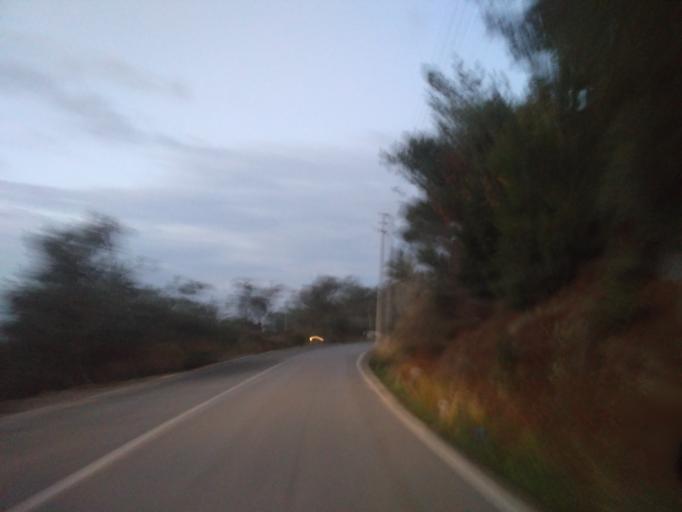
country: TR
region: Izmir
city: Buca
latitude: 38.3572
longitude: 27.2627
